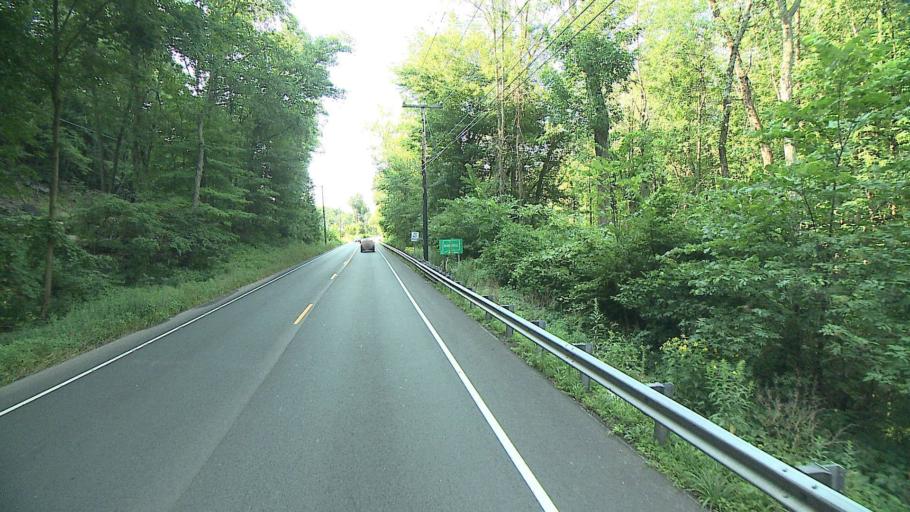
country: US
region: Connecticut
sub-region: Fairfield County
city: Georgetown
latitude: 41.2720
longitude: -73.4432
